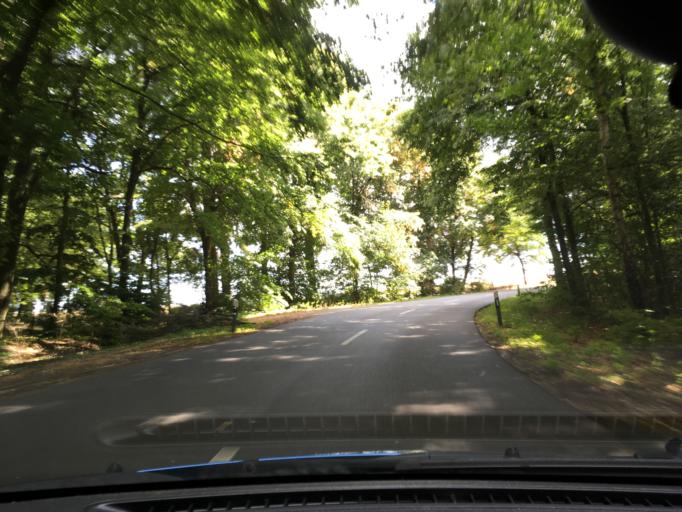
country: DE
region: Lower Saxony
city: Rehlingen
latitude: 53.0751
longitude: 10.2323
